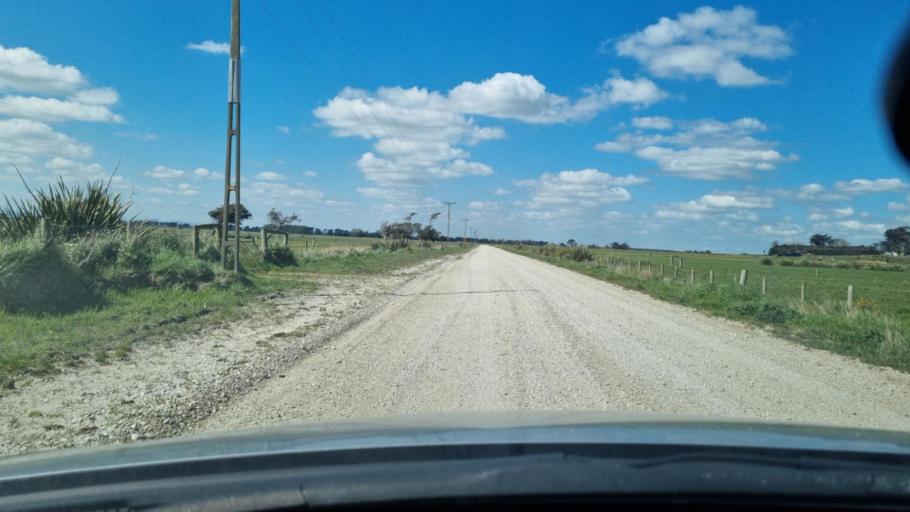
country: NZ
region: Southland
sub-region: Invercargill City
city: Invercargill
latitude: -46.3927
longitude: 168.2491
